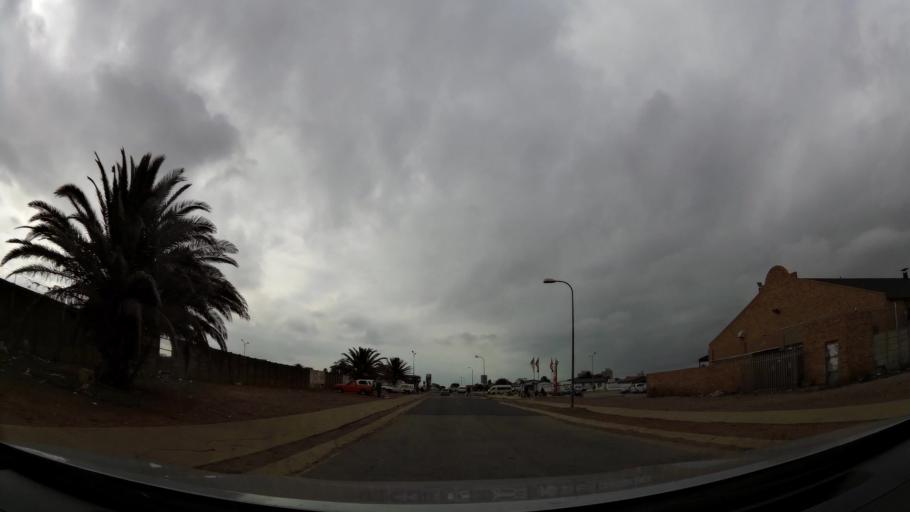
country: ZA
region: Eastern Cape
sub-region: Nelson Mandela Bay Metropolitan Municipality
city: Port Elizabeth
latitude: -33.9032
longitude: 25.5604
